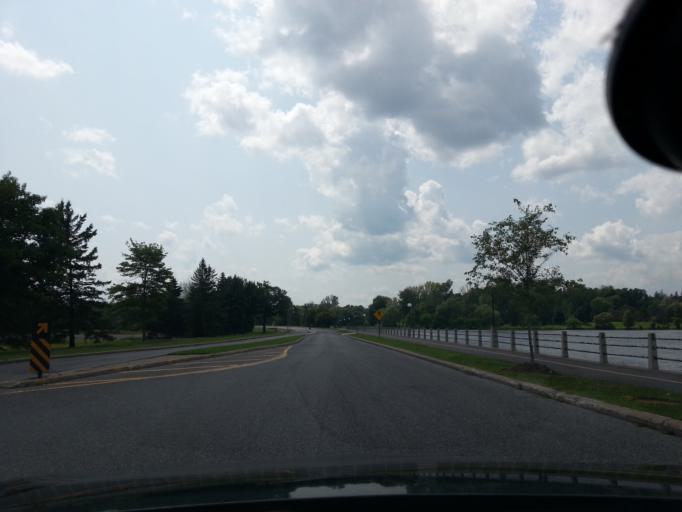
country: CA
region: Ontario
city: Ottawa
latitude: 45.3932
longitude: -75.6974
